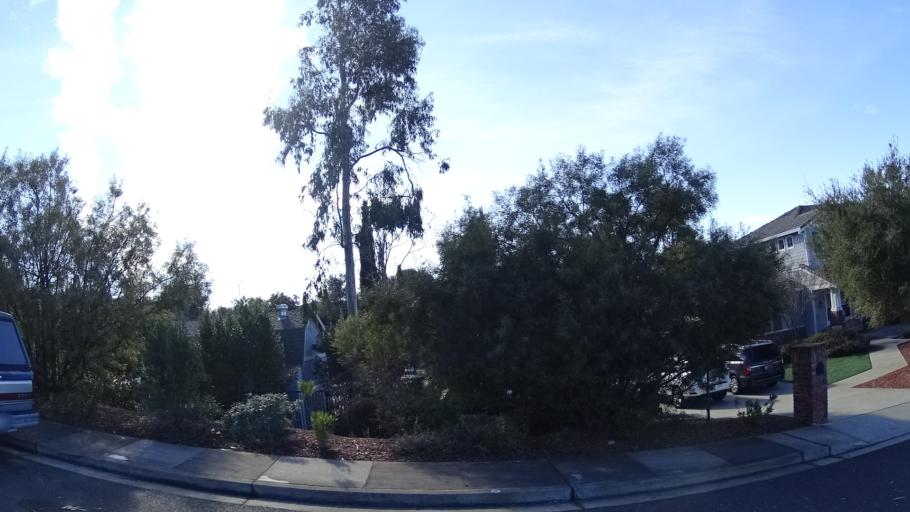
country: US
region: California
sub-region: Alameda County
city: Fairview
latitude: 37.6773
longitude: -122.0377
